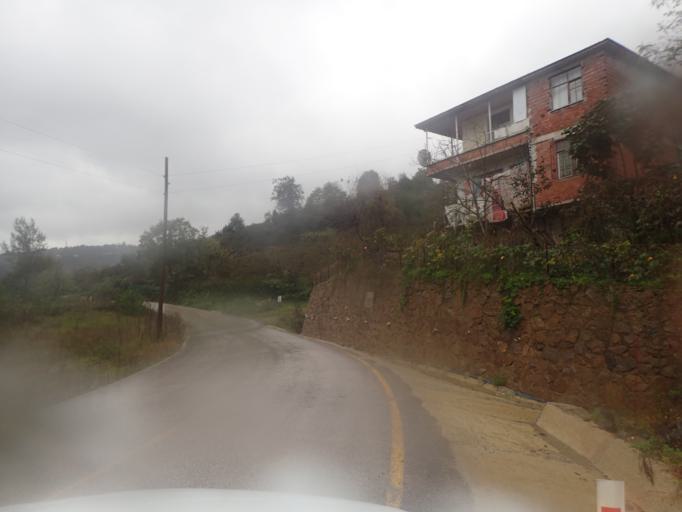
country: TR
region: Ordu
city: Persembe
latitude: 41.0473
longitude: 37.7512
